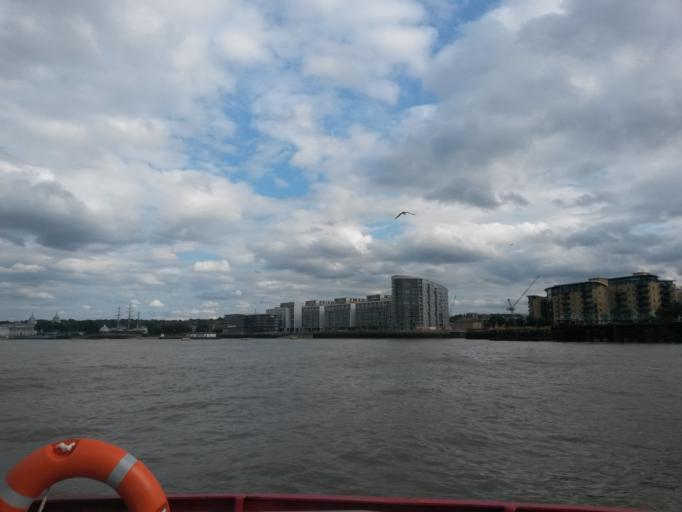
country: GB
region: England
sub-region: Greater London
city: Poplar
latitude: 51.4861
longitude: -0.0216
